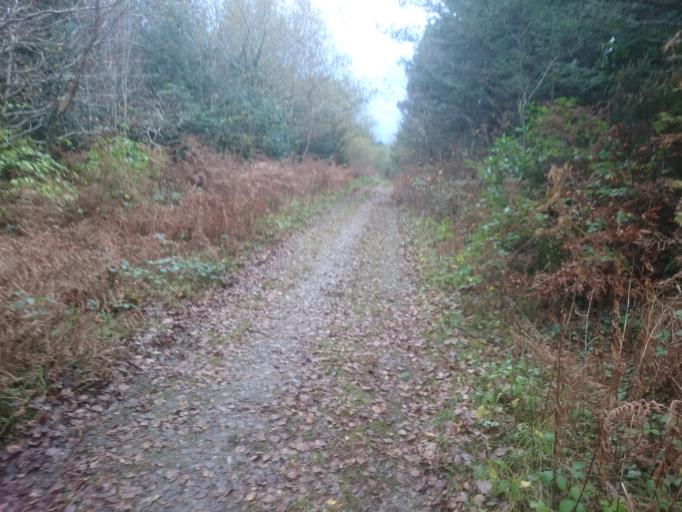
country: IE
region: Leinster
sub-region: Kilkenny
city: Thomastown
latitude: 52.4645
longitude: -7.0522
